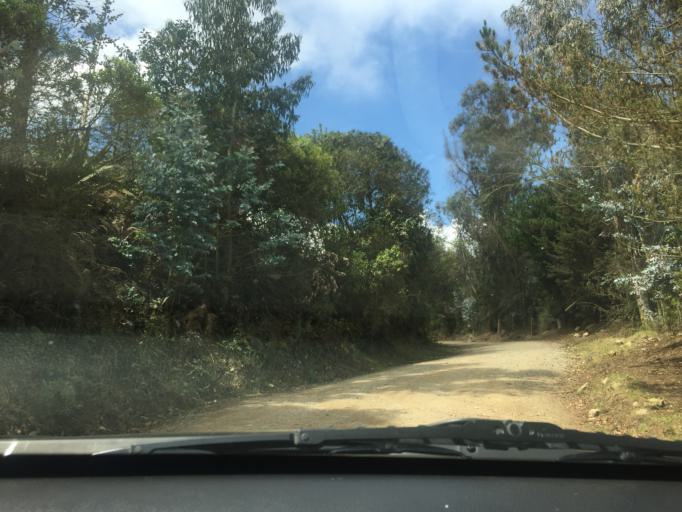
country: CO
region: Cundinamarca
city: Zipacon
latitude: 4.7872
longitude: -74.3779
